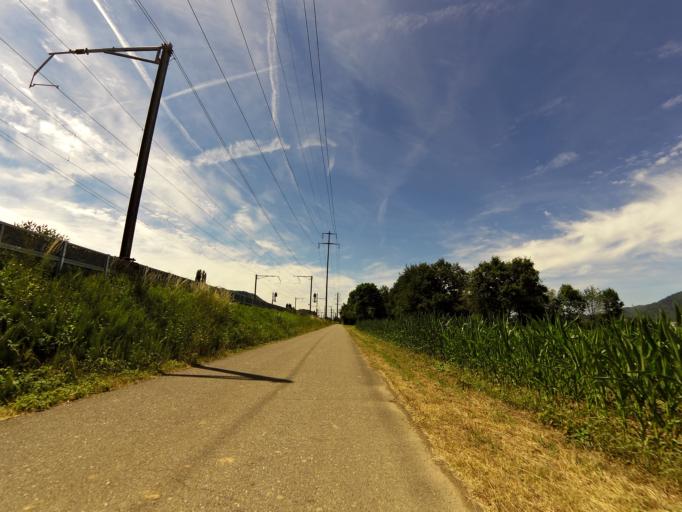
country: CH
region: Aargau
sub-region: Bezirk Rheinfelden
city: Stein
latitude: 47.5399
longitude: 7.9693
